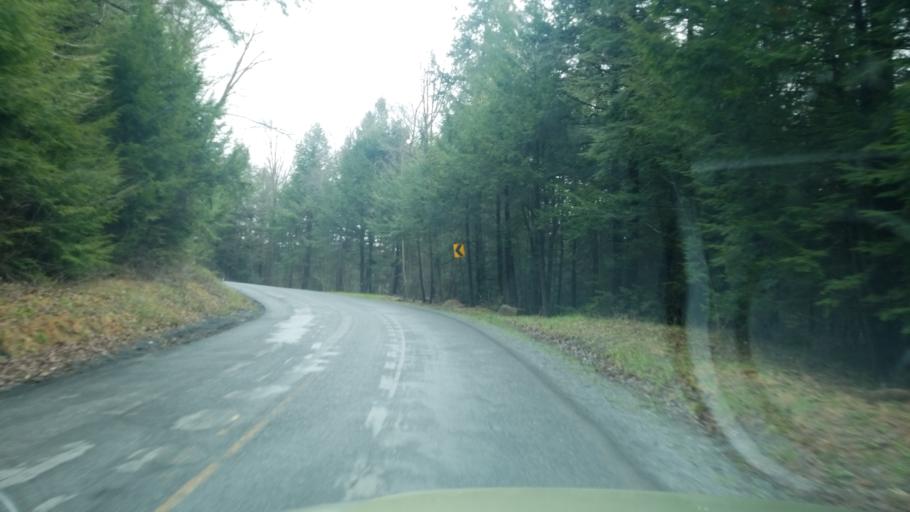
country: US
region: Pennsylvania
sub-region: Clearfield County
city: Clearfield
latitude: 41.0617
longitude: -78.4194
